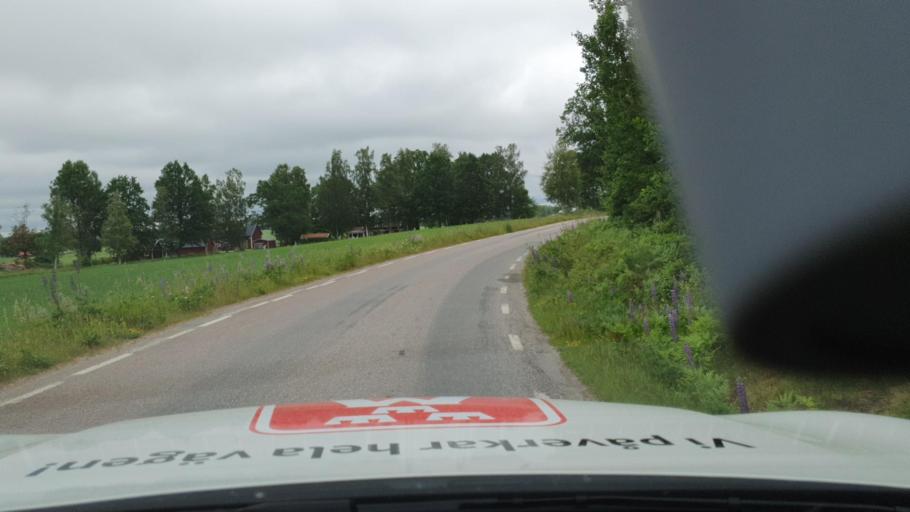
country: SE
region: Vaestra Goetaland
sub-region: Tibro Kommun
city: Tibro
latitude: 58.3555
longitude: 14.1577
